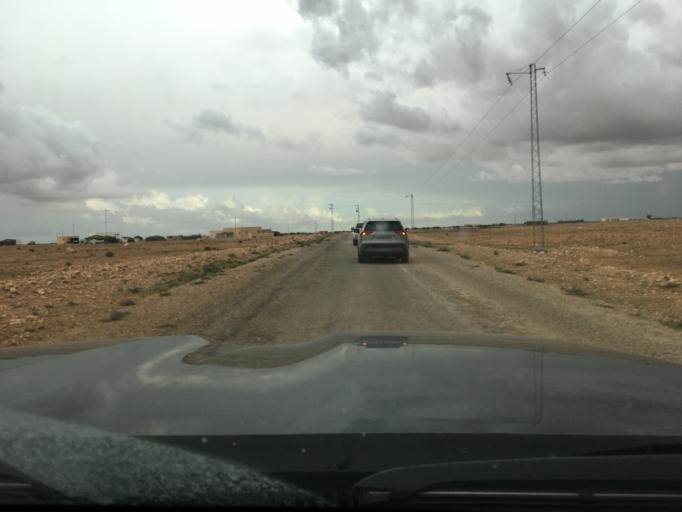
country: TN
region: Madanin
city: Medenine
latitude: 33.2910
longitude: 10.6065
